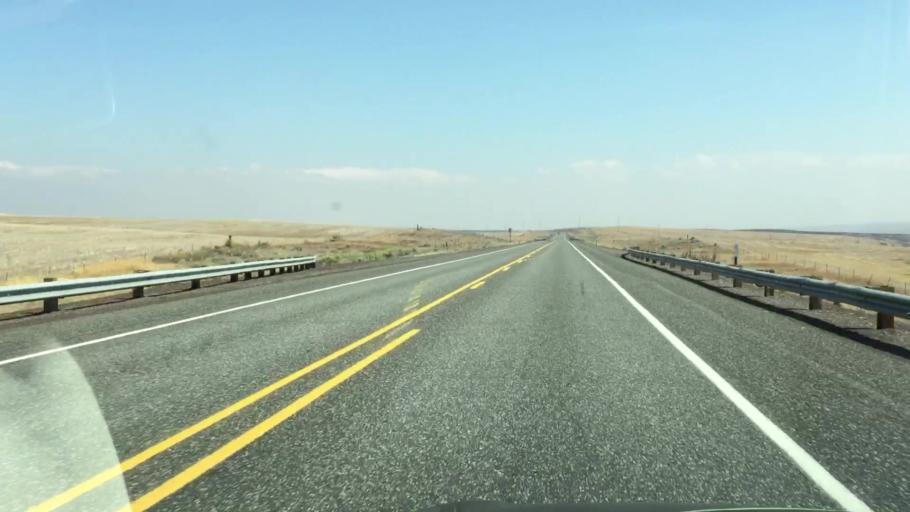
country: US
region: Oregon
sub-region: Wasco County
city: The Dalles
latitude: 45.3275
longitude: -121.1486
